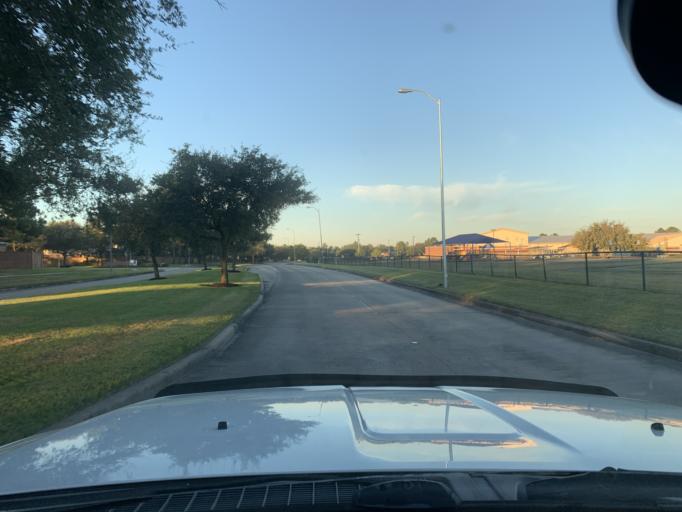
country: US
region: Texas
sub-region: Fort Bend County
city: Four Corners
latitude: 29.6492
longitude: -95.6416
